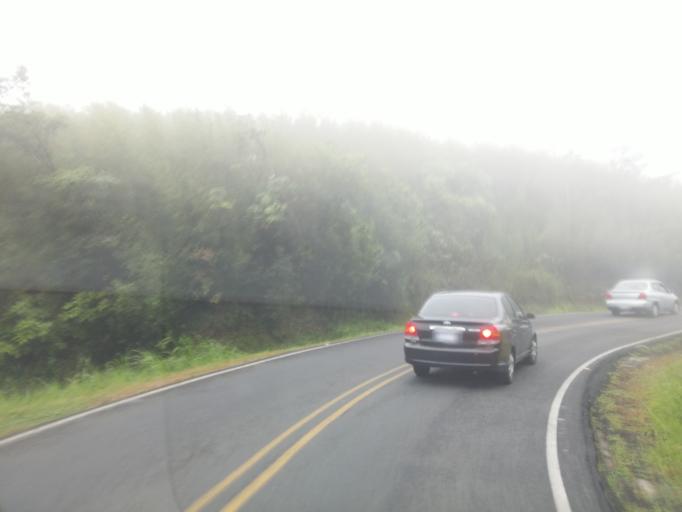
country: CR
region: Alajuela
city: San Ramon
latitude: 10.1796
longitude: -84.5048
